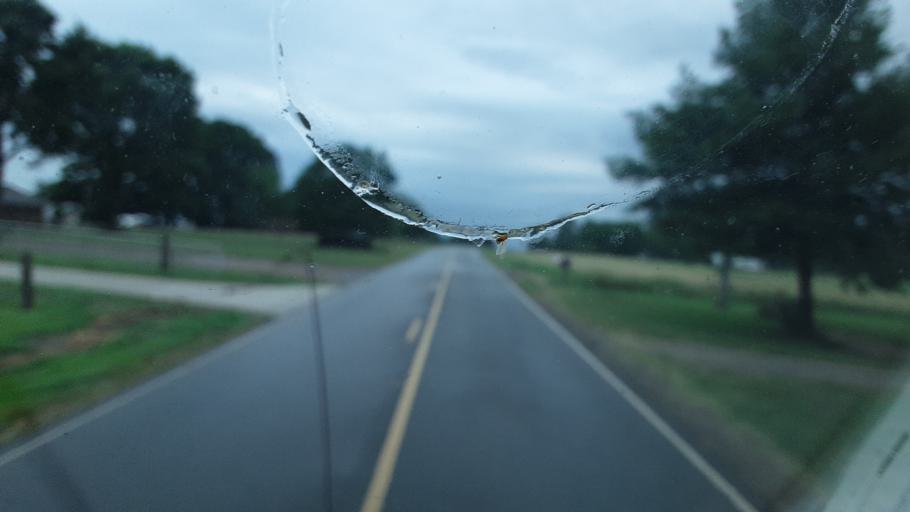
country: US
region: North Carolina
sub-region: Yadkin County
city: Jonesville
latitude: 36.0635
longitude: -80.8323
